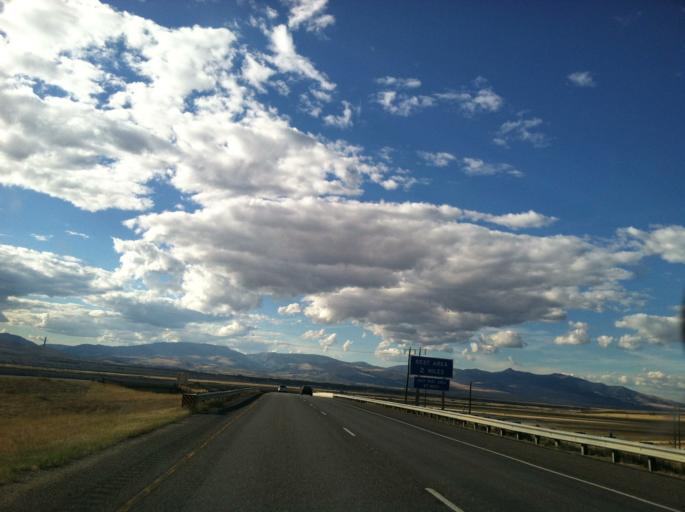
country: US
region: Montana
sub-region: Deer Lodge County
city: Warm Springs
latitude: 46.0646
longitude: -112.7727
